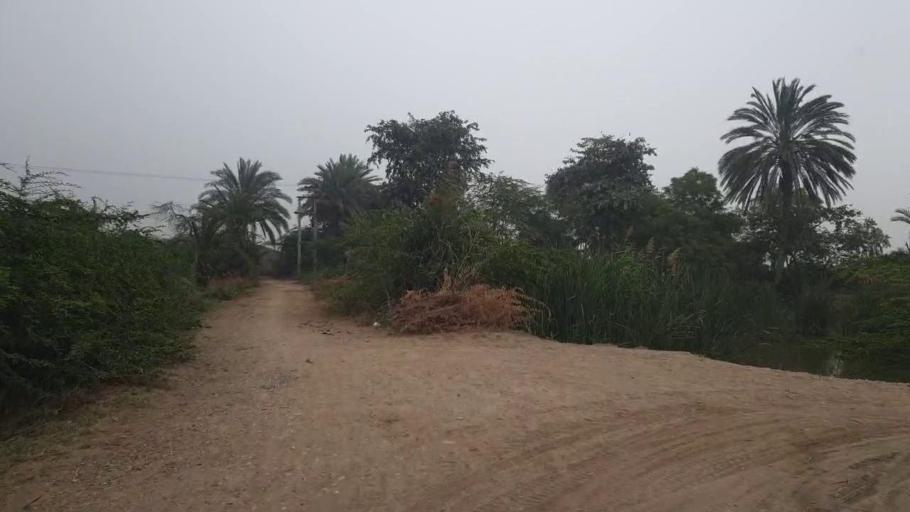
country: PK
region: Sindh
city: Badin
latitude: 24.6274
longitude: 68.7017
